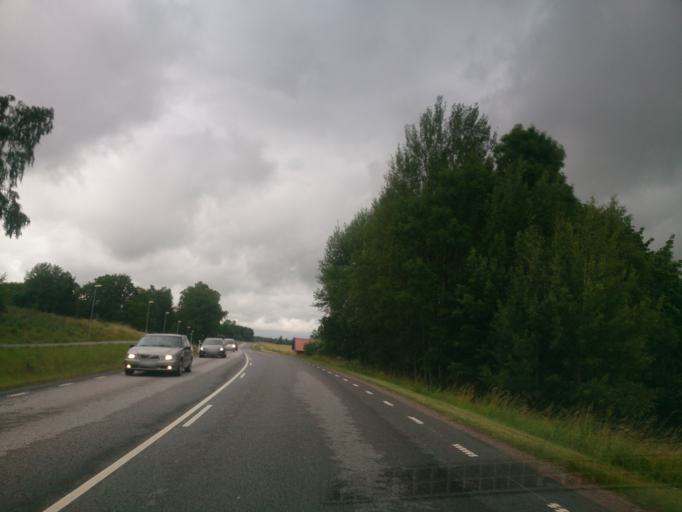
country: SE
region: OEstergoetland
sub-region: Linkopings Kommun
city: Malmslatt
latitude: 58.4250
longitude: 15.5655
